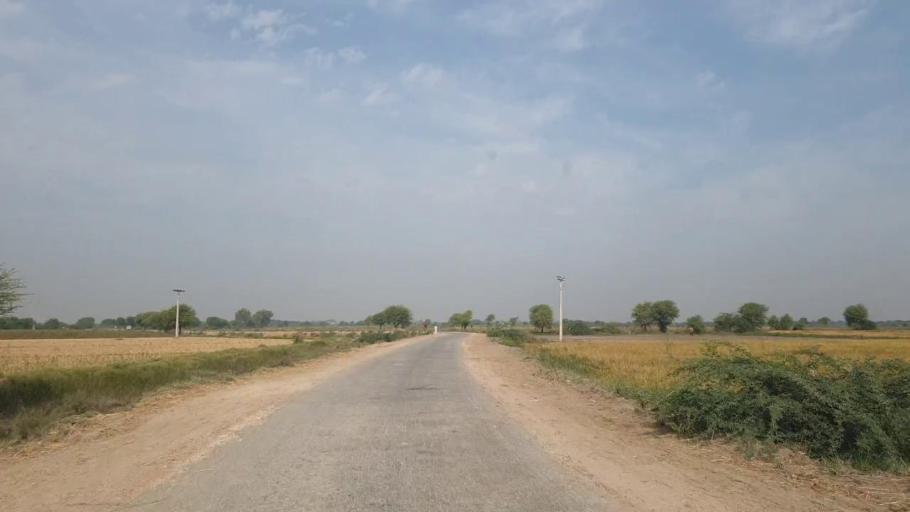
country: PK
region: Sindh
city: Rajo Khanani
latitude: 24.9390
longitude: 68.9843
